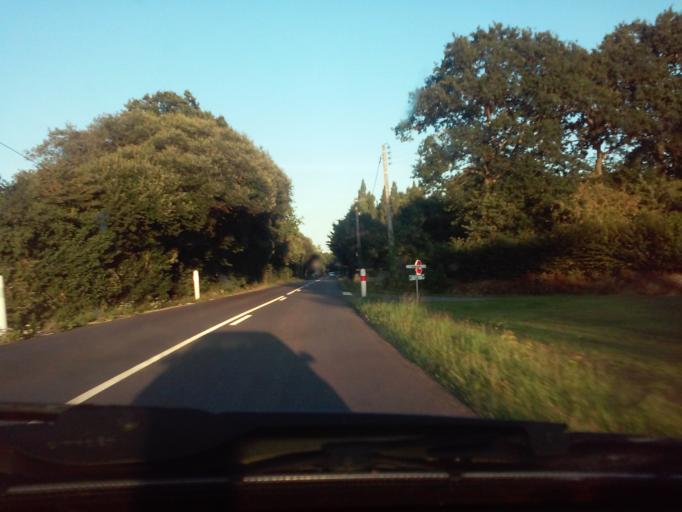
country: FR
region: Brittany
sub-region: Departement d'Ille-et-Vilaine
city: Saint-Pierre-de-Plesguen
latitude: 48.4350
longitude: -1.9348
